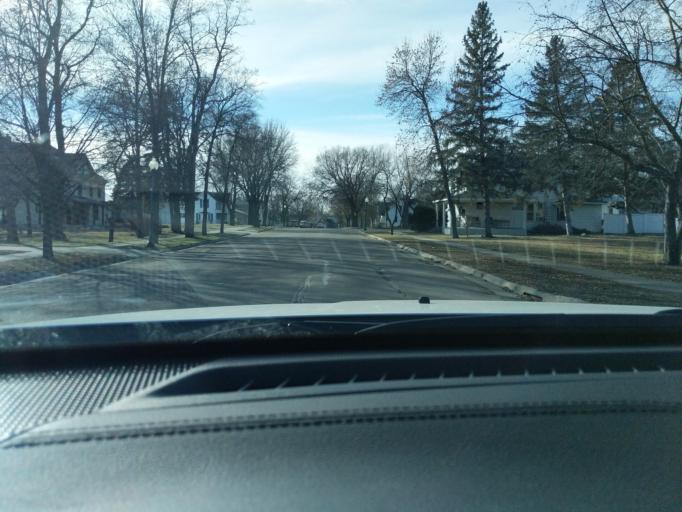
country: US
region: Minnesota
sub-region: Yellow Medicine County
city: Granite Falls
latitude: 44.8080
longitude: -95.5409
